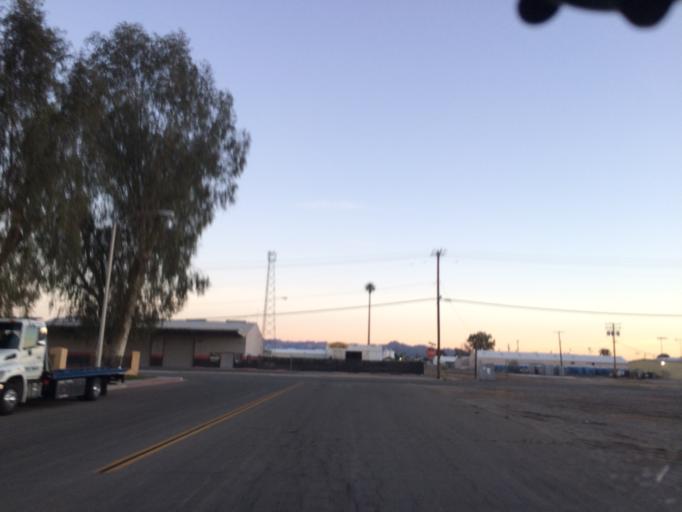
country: US
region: California
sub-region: Riverside County
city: Blythe
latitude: 33.6134
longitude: -114.6009
